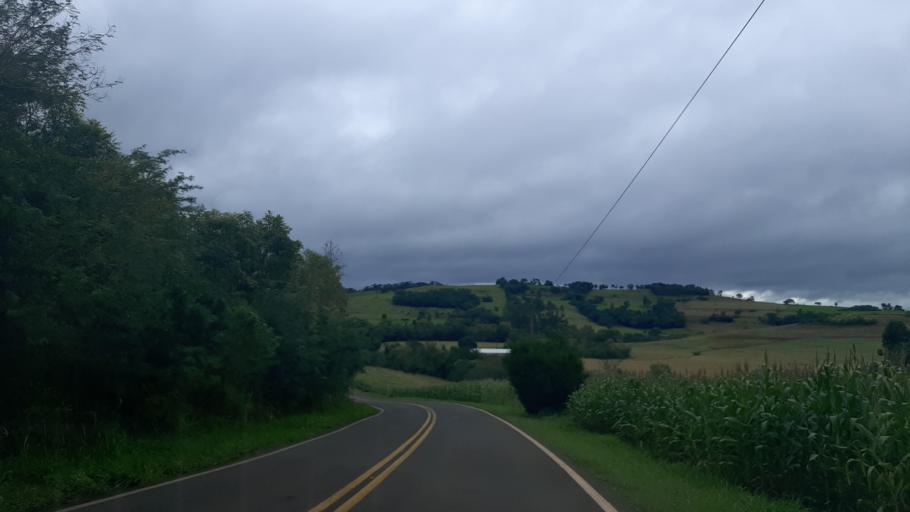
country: BR
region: Parana
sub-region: Ampere
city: Ampere
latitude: -25.9960
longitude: -53.4389
